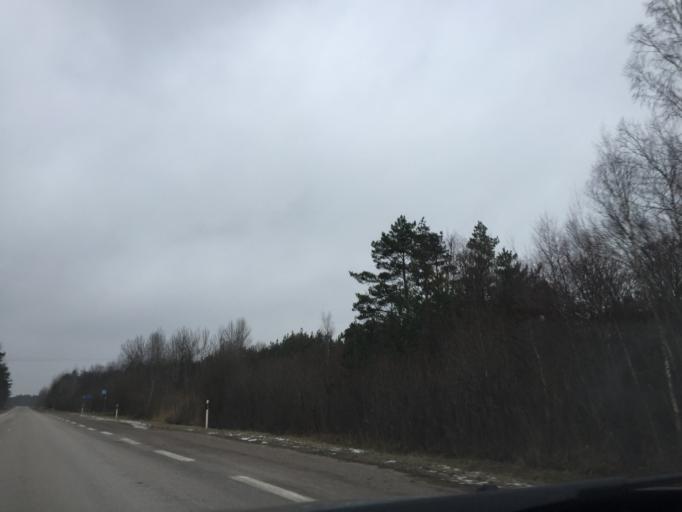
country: EE
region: Saare
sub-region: Kuressaare linn
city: Kuressaare
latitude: 58.2802
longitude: 22.4319
